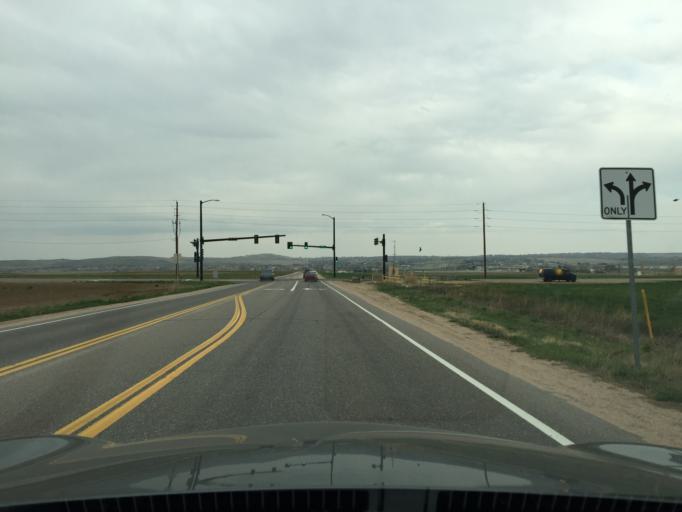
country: US
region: Colorado
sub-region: Boulder County
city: Lafayette
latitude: 40.0149
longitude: -105.0757
